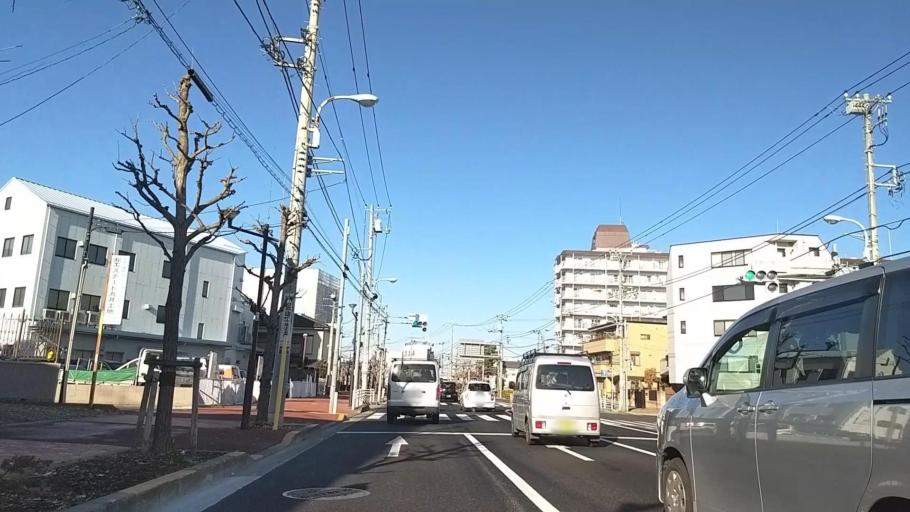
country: JP
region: Tokyo
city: Chofugaoka
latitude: 35.6410
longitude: 139.5192
